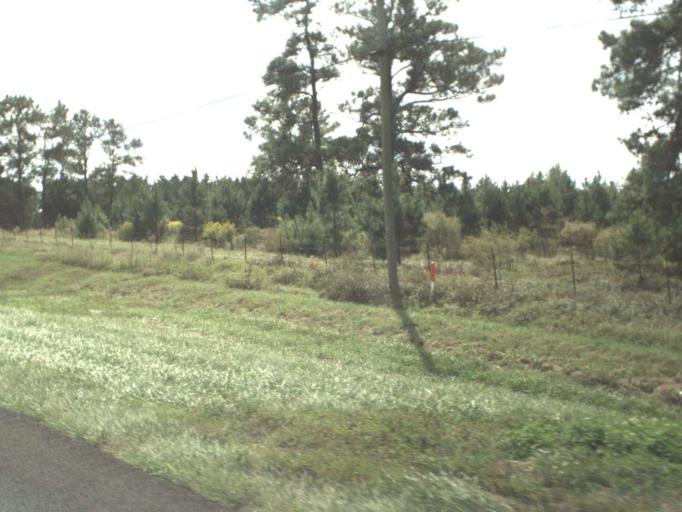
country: US
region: Florida
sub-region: Jackson County
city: Graceville
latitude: 30.9105
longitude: -85.3783
